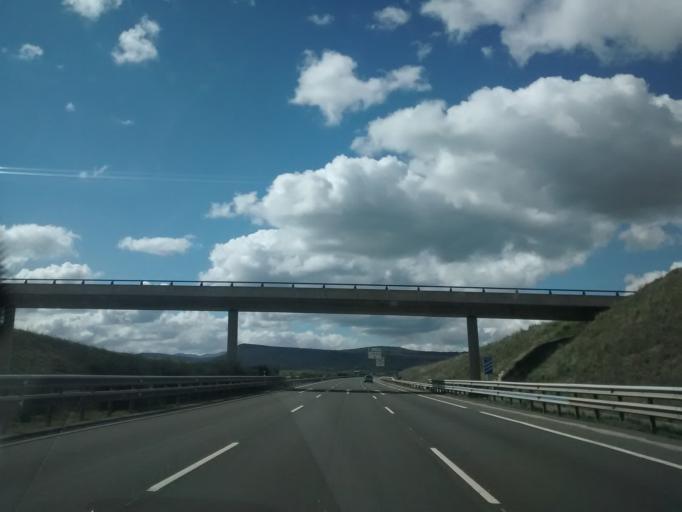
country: ES
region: Basque Country
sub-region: Provincia de Alava
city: Arminon
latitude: 42.7688
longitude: -2.8228
